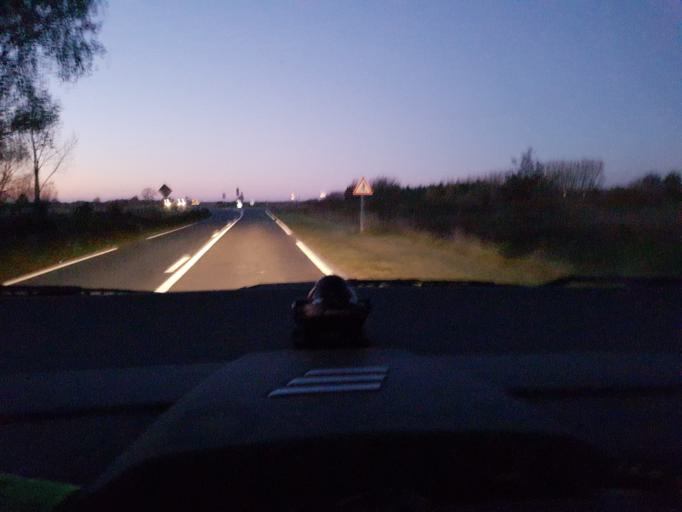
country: FR
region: Picardie
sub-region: Departement de la Somme
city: Pende
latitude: 50.1987
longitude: 1.5549
